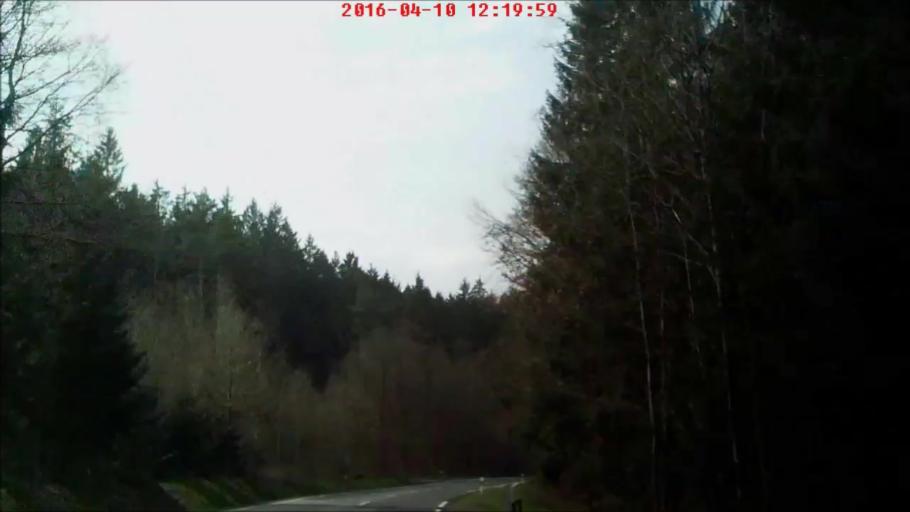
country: DE
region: Thuringia
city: Benshausen
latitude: 50.6570
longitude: 10.5944
